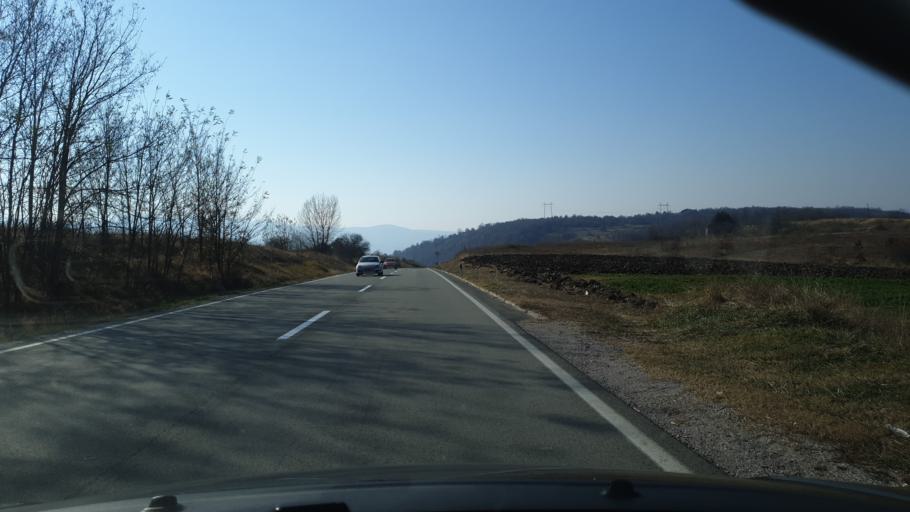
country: RS
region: Central Serbia
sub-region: Nisavski Okrug
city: Svrljig
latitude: 43.4420
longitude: 22.1702
